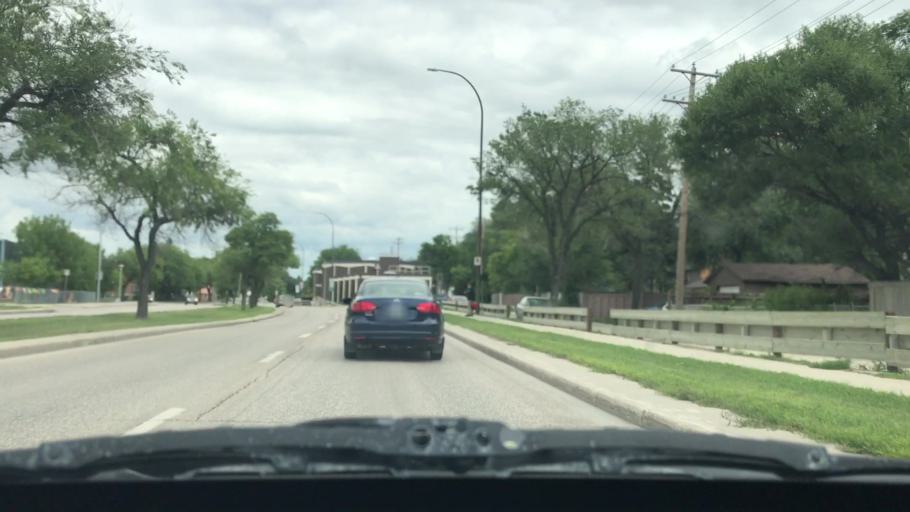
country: CA
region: Manitoba
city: Winnipeg
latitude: 49.8512
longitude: -97.1153
